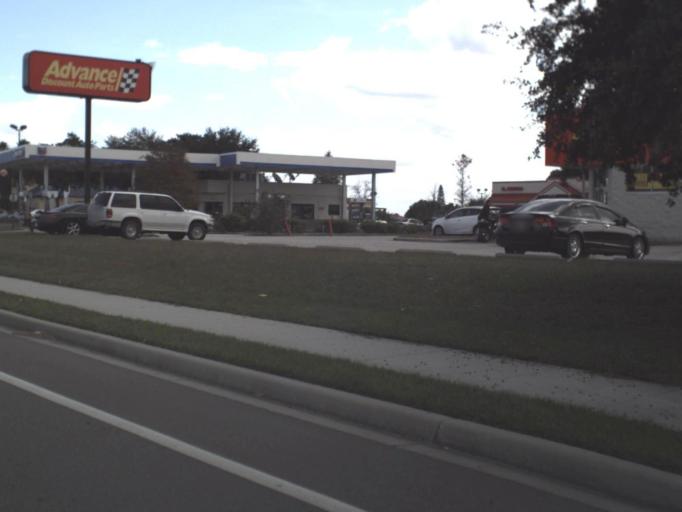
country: US
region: Florida
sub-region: Osceola County
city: Buenaventura Lakes
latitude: 28.3454
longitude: -81.3673
